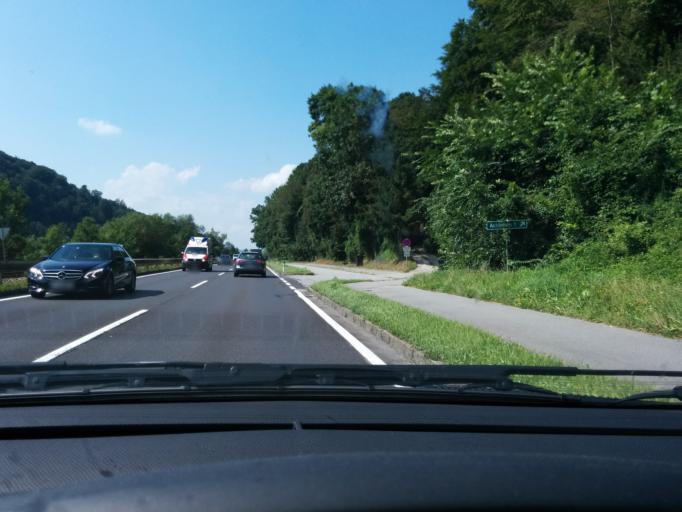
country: AT
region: Upper Austria
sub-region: Politischer Bezirk Urfahr-Umgebung
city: Ottensheim
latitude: 48.3146
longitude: 14.2150
